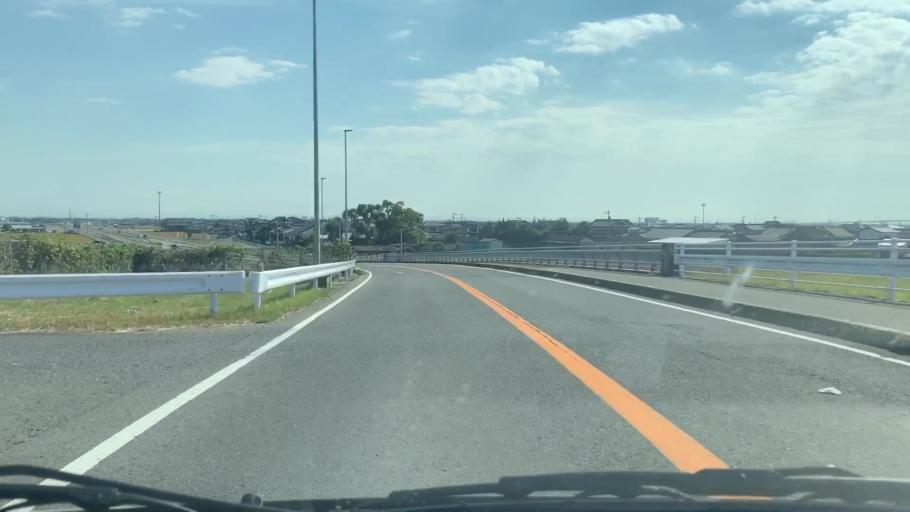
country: JP
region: Saga Prefecture
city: Saga-shi
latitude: 33.2218
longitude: 130.1945
